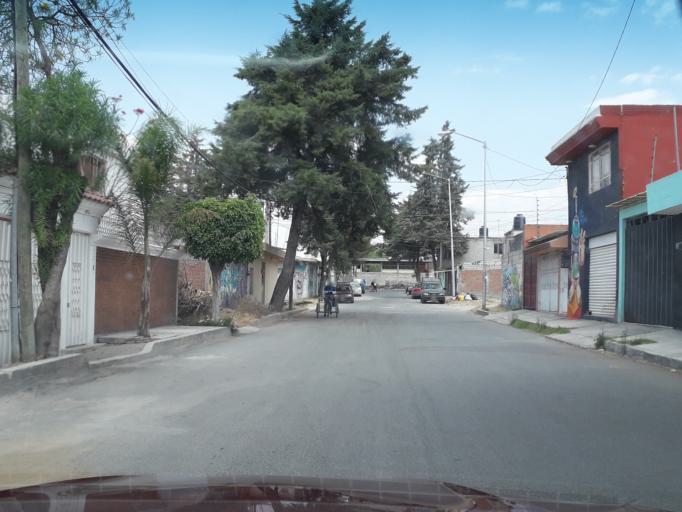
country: MX
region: Puebla
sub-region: Puebla
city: El Capulo (La Quebradora)
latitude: 18.9671
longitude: -98.2600
